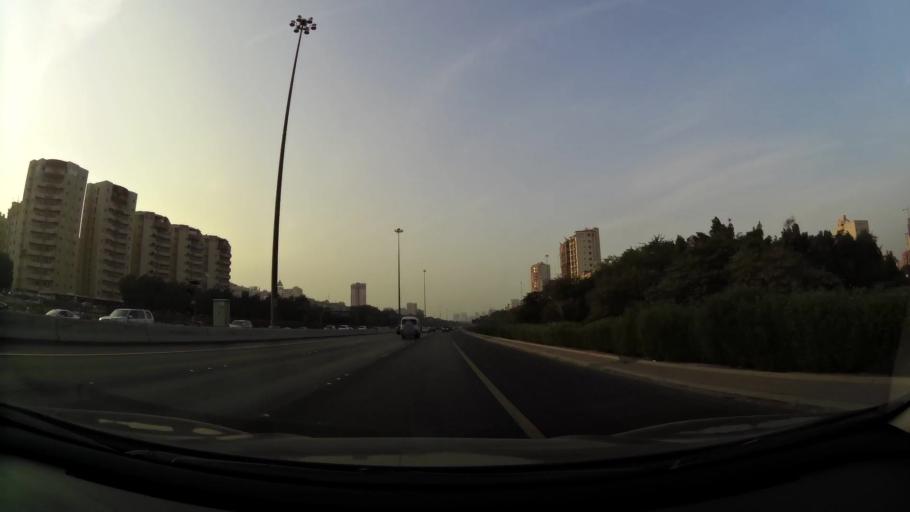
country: KW
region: Muhafazat Hawalli
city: Hawalli
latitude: 29.3319
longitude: 48.0392
